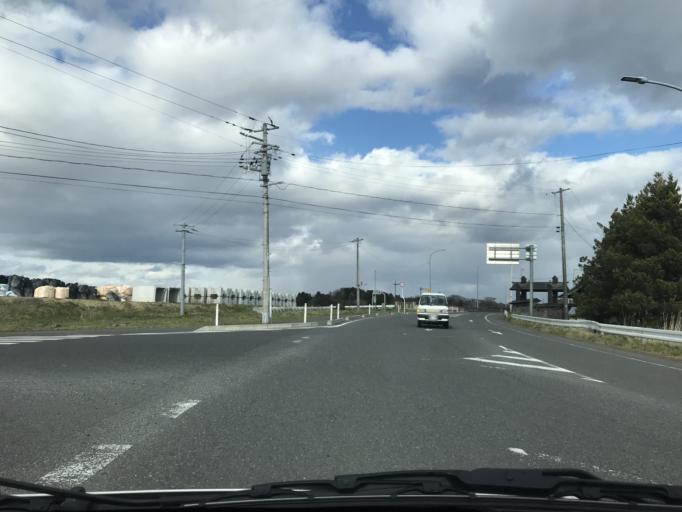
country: JP
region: Miyagi
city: Wakuya
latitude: 38.6267
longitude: 141.2057
